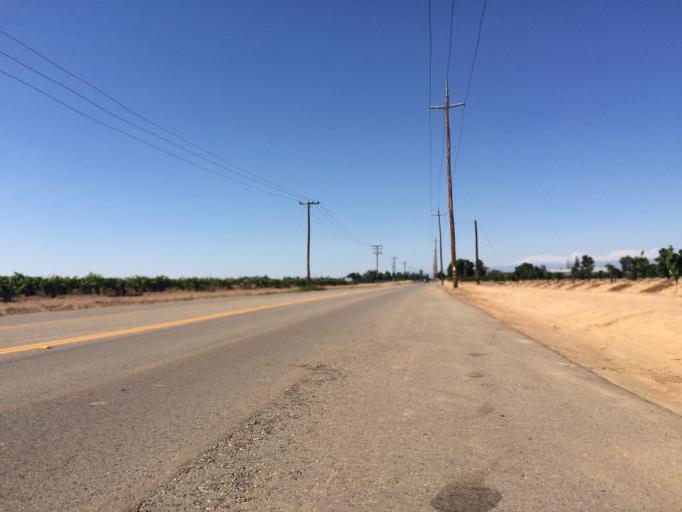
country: US
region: California
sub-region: Fresno County
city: Sanger
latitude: 36.7377
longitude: -119.6100
